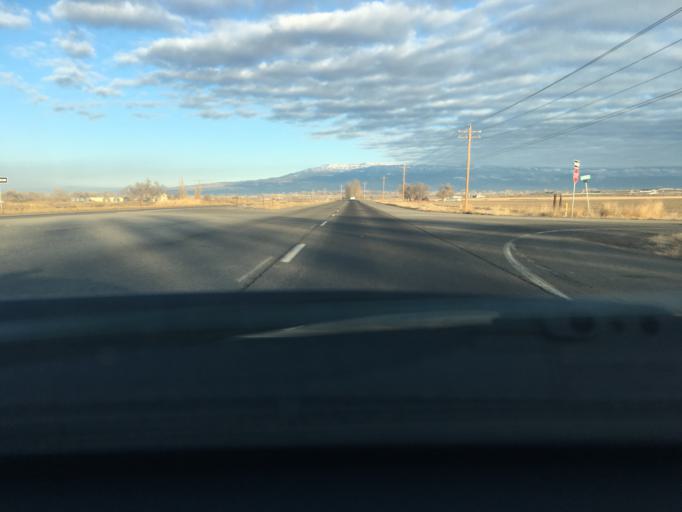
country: US
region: Colorado
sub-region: Delta County
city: Delta
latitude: 38.6856
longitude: -108.0109
